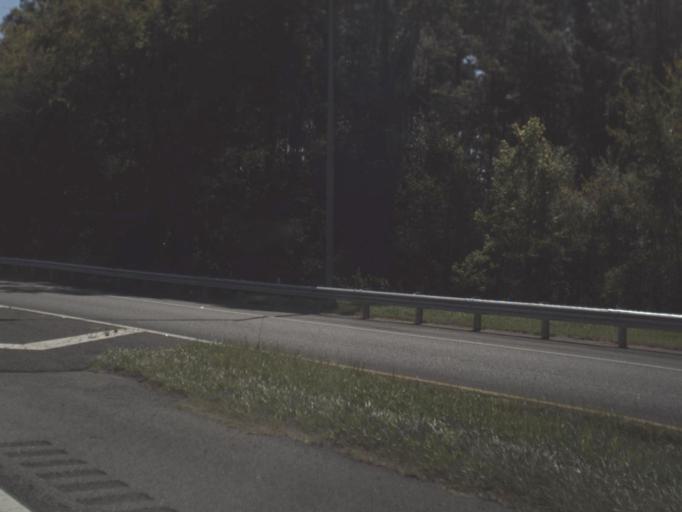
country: US
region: Florida
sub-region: Sumter County
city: Wildwood
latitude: 28.8353
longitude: -82.0426
